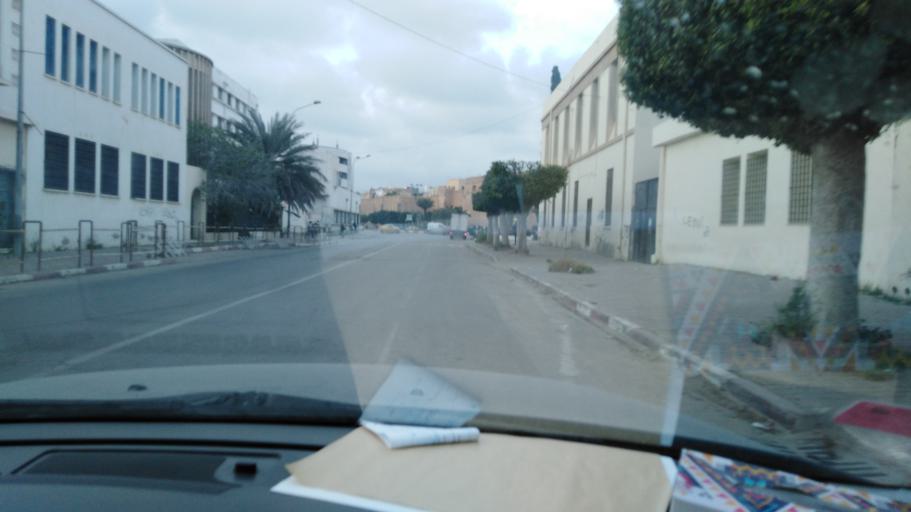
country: TN
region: Safaqis
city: Sfax
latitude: 34.7320
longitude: 10.7585
